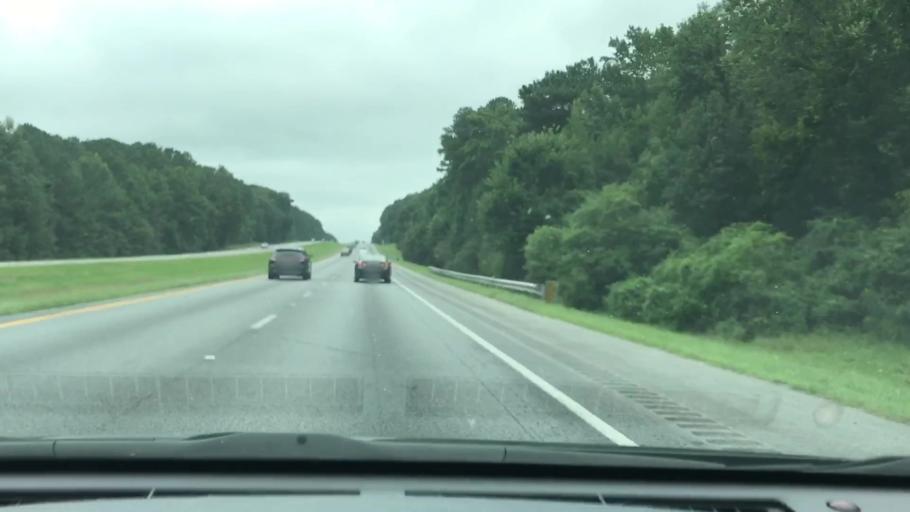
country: US
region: Georgia
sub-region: Morgan County
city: Madison
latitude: 33.5827
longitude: -83.5924
